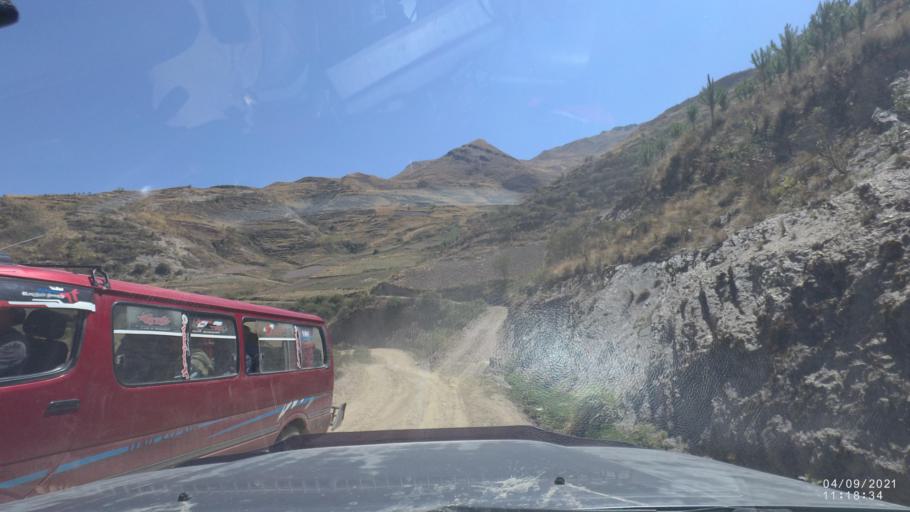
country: BO
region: Cochabamba
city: Sipe Sipe
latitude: -17.2665
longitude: -66.4936
